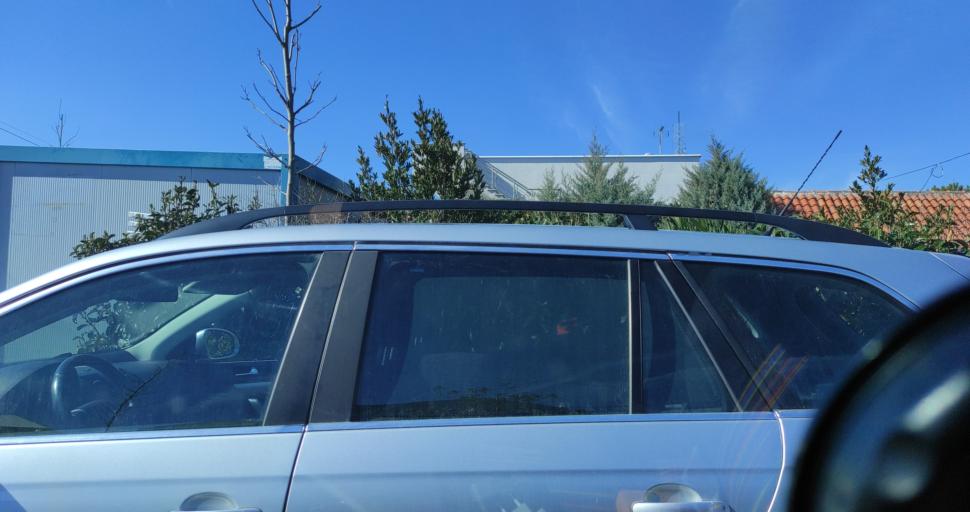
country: AL
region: Shkoder
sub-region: Rrethi i Shkodres
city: Velipoje
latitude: 41.8630
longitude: 19.4150
